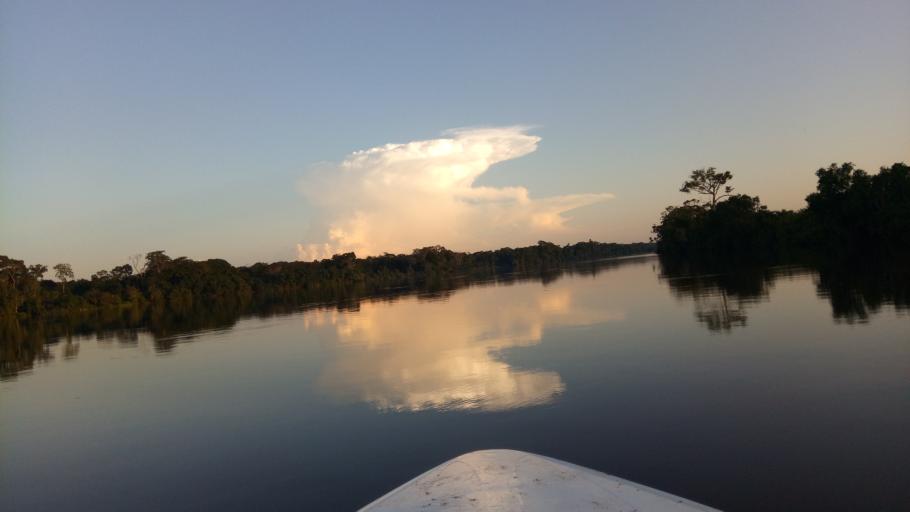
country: CD
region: Eastern Province
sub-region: Sous-Region de la Tshopo
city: Yangambi
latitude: 0.0036
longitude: 24.0248
